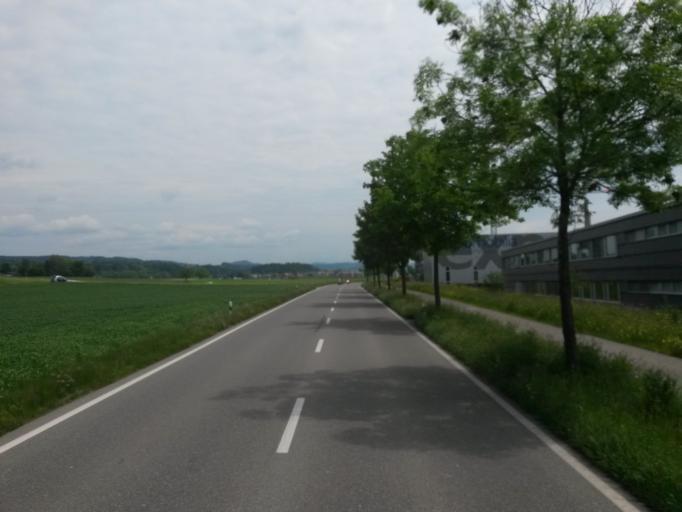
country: CH
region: Zurich
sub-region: Bezirk Pfaeffikon
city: Illnau / Unter-Illnau
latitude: 47.3967
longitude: 8.7375
